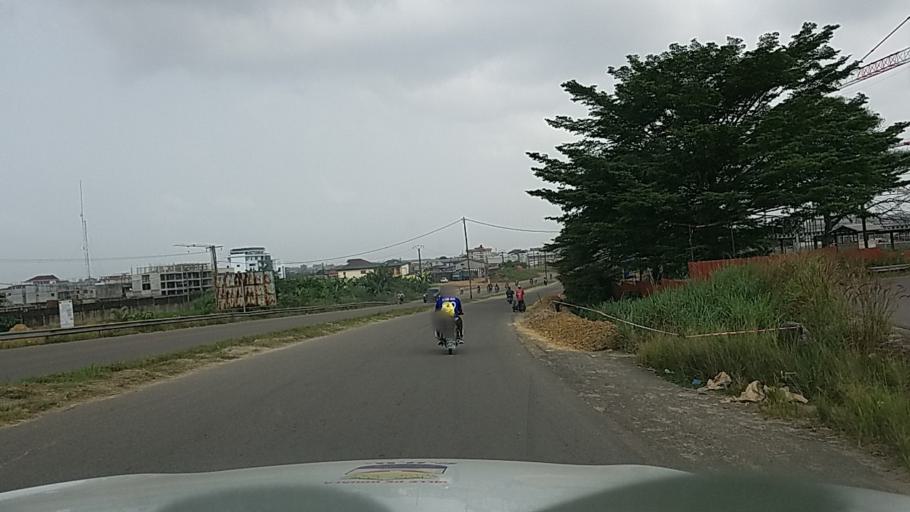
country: CM
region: Littoral
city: Douala
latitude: 4.0219
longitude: 9.7185
